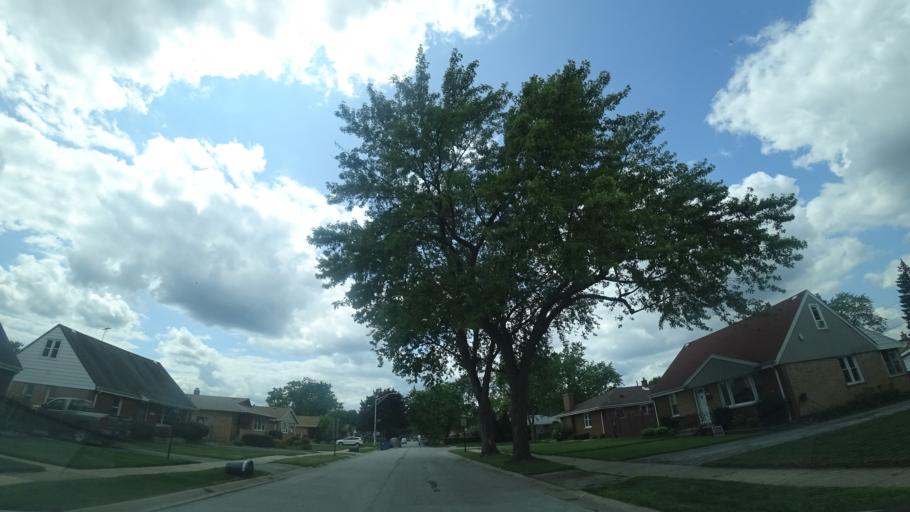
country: US
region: Illinois
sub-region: Cook County
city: Alsip
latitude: 41.6805
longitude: -87.7308
